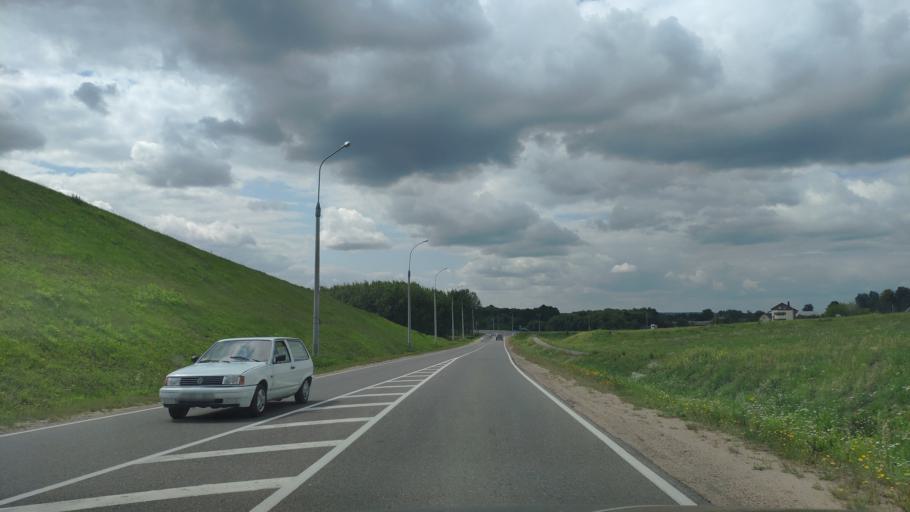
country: BY
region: Minsk
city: Zaslawye
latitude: 54.0062
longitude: 27.3088
